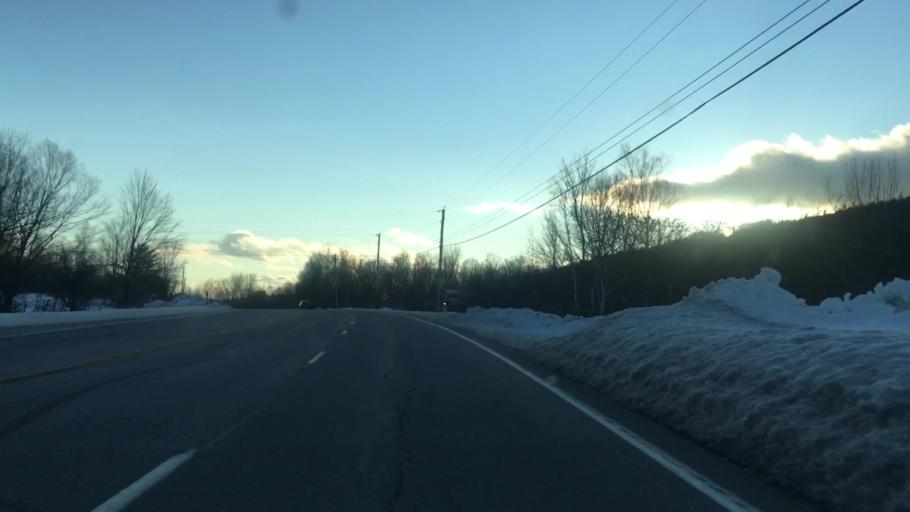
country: US
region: Maine
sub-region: Oxford County
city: Peru
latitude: 44.5852
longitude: -70.3683
